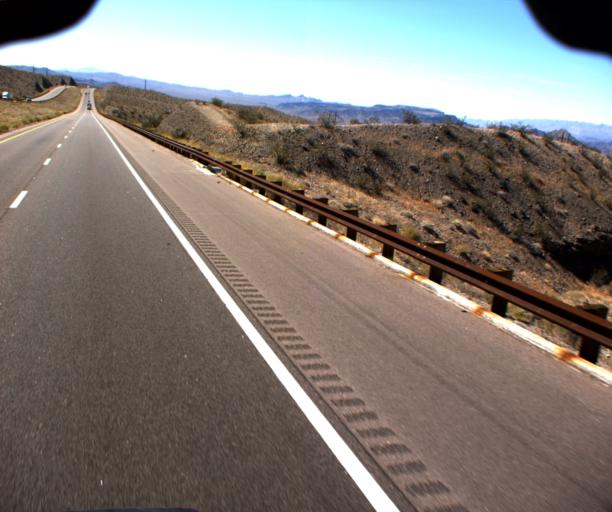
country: US
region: Nevada
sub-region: Clark County
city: Boulder City
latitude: 35.9244
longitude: -114.6330
